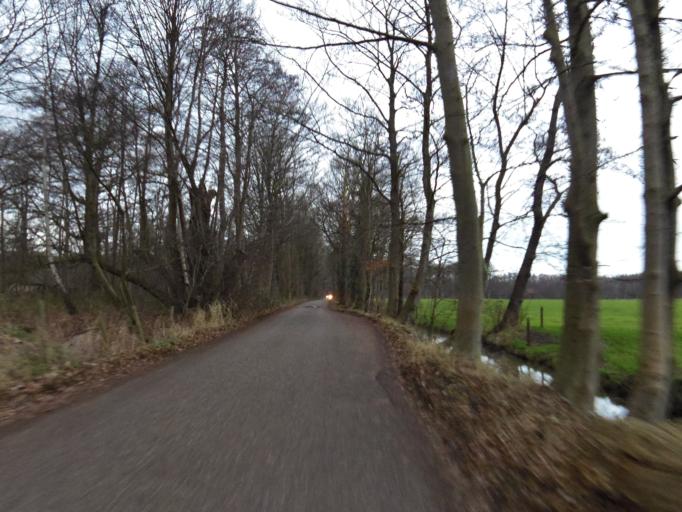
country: NL
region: North Holland
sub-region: Gemeente Bloemendaal
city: Bennebroek
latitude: 52.3296
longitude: 4.5721
